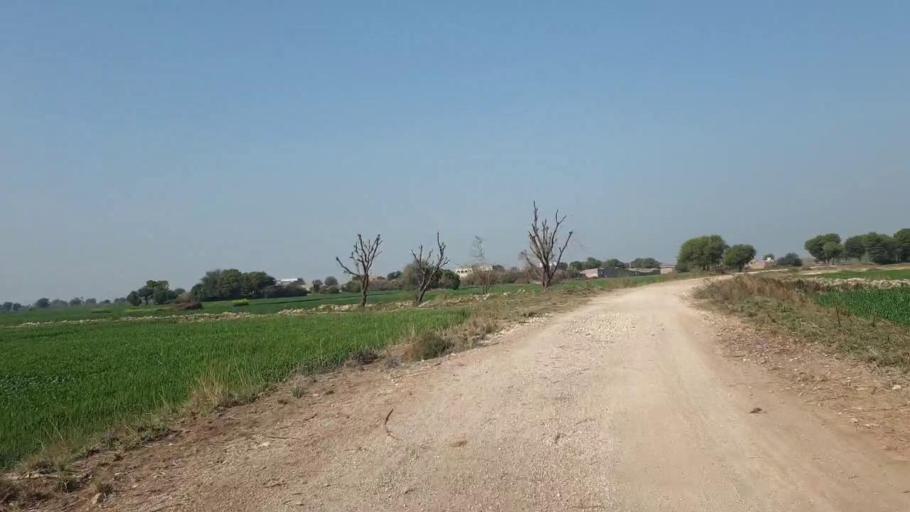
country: PK
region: Sindh
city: Hala
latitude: 25.9226
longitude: 68.4080
